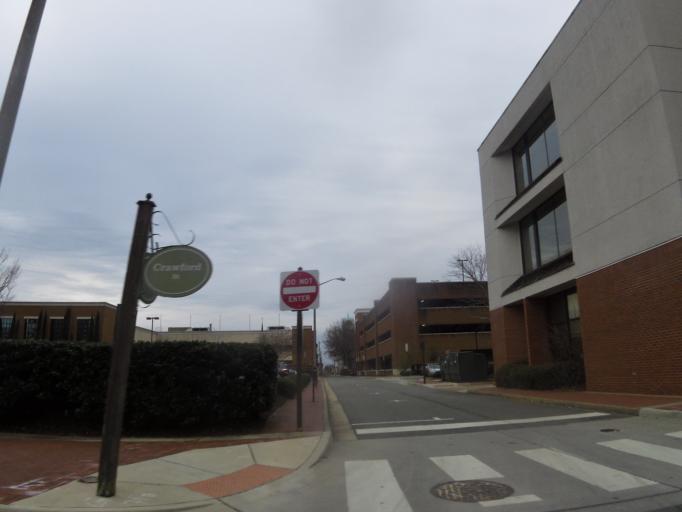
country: US
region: Virginia
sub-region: City of Portsmouth
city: Portsmouth
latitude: 36.8363
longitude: -76.2980
